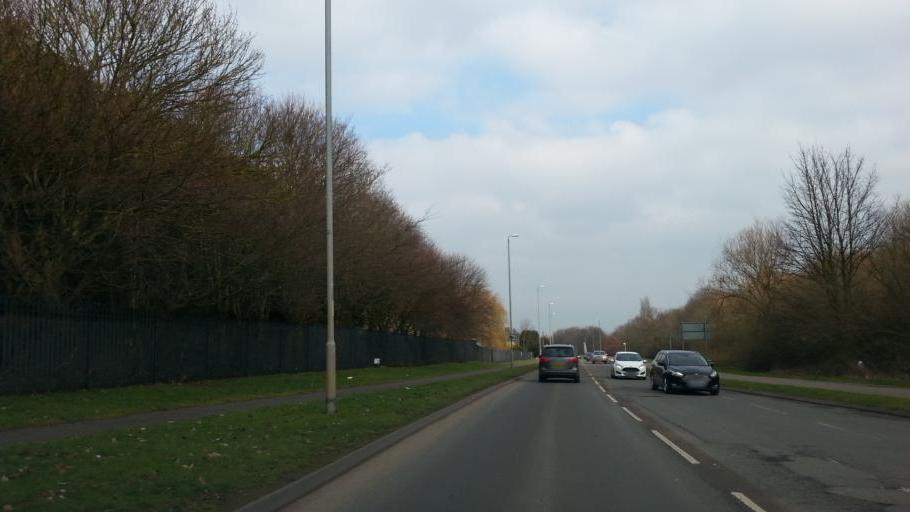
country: GB
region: England
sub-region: Northamptonshire
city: Corby
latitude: 52.4776
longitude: -0.7102
